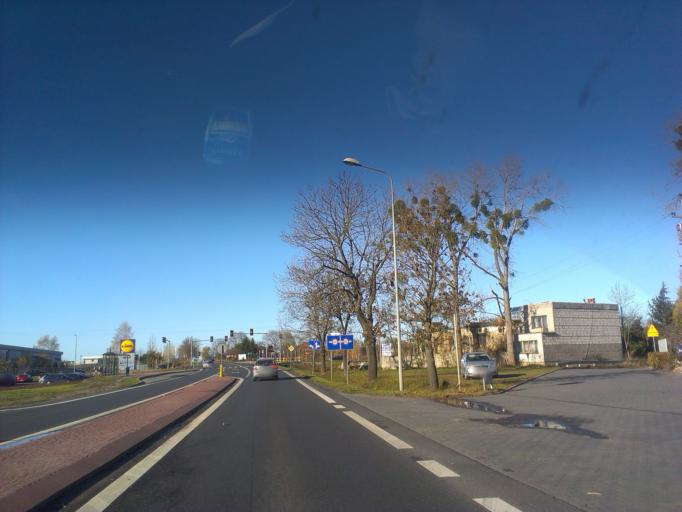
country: PL
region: Greater Poland Voivodeship
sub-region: Powiat poznanski
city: Suchy Las
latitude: 52.4775
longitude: 16.8705
